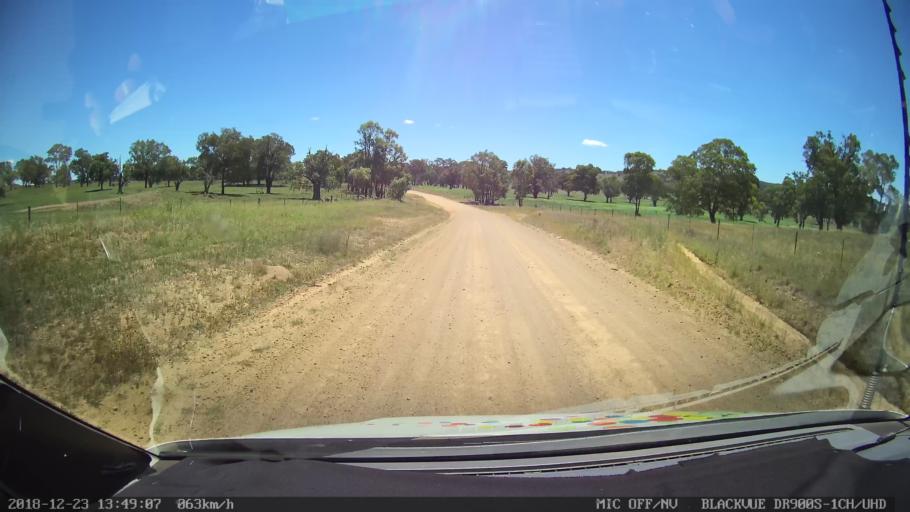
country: AU
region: New South Wales
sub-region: Tamworth Municipality
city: Manilla
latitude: -30.5202
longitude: 151.1108
